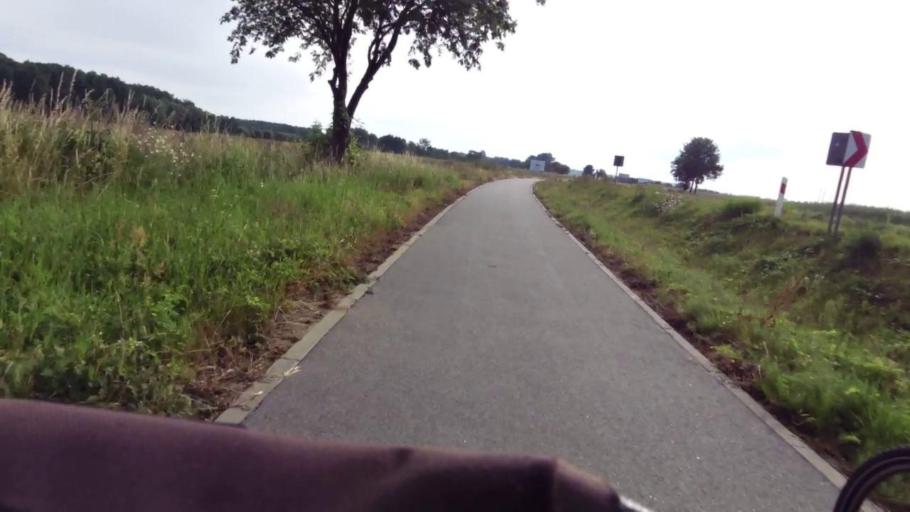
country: PL
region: West Pomeranian Voivodeship
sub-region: Powiat kamienski
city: Kamien Pomorski
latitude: 53.9883
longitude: 14.8023
